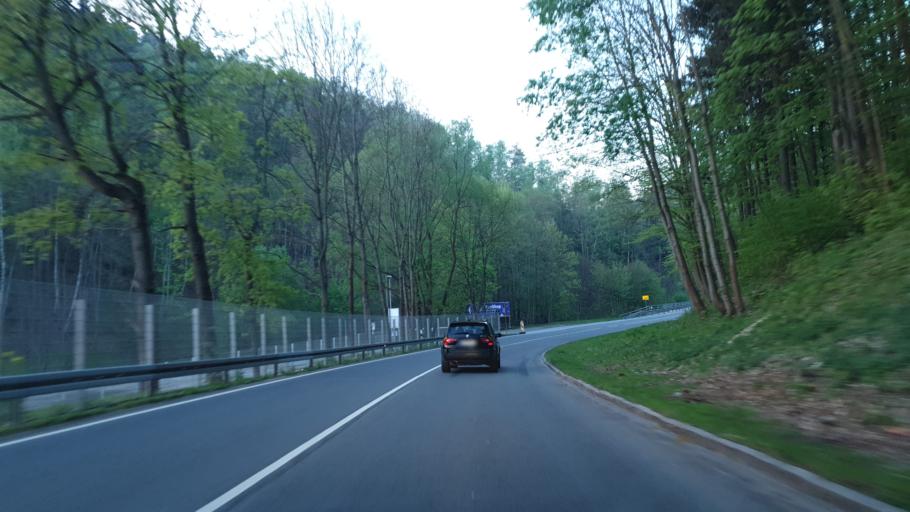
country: DE
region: Saxony
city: Aue
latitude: 50.5988
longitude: 12.7139
